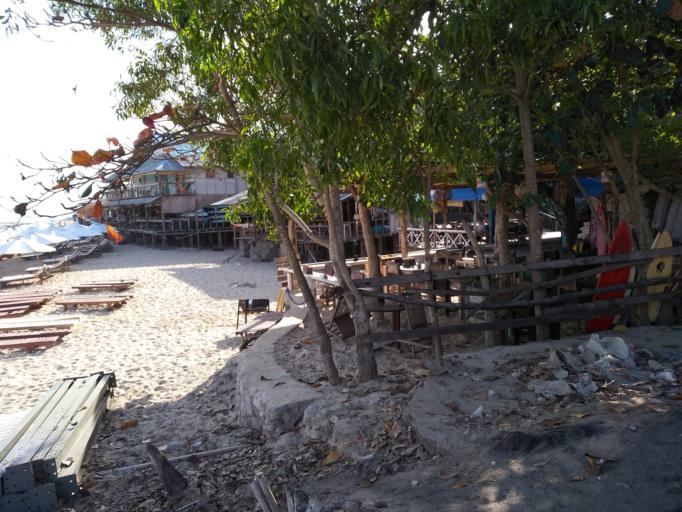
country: ID
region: Bali
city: Jimbaran
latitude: -8.7936
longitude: 115.1224
